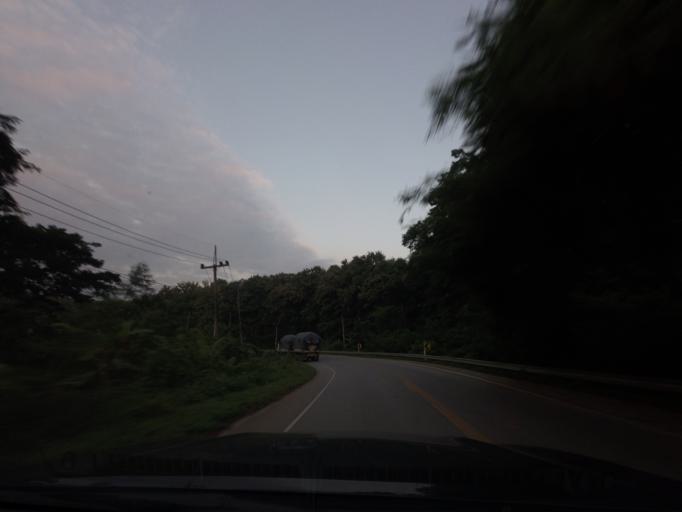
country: TH
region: Nan
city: Wiang Sa
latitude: 18.4731
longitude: 100.7226
